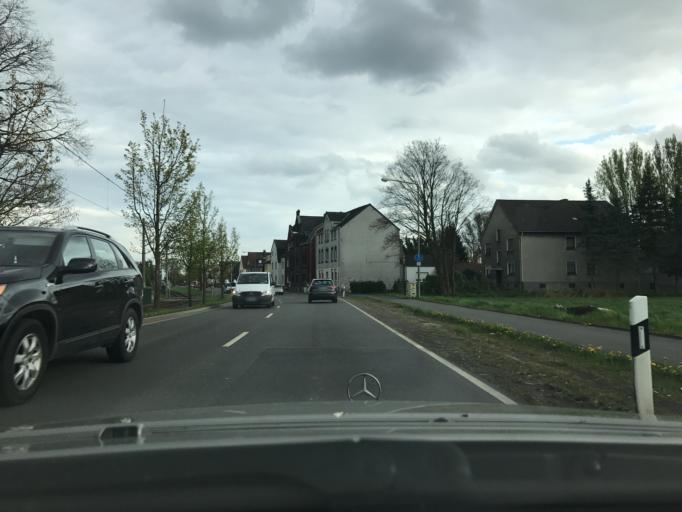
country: DE
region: North Rhine-Westphalia
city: Waltrop
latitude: 51.5840
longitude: 7.4501
